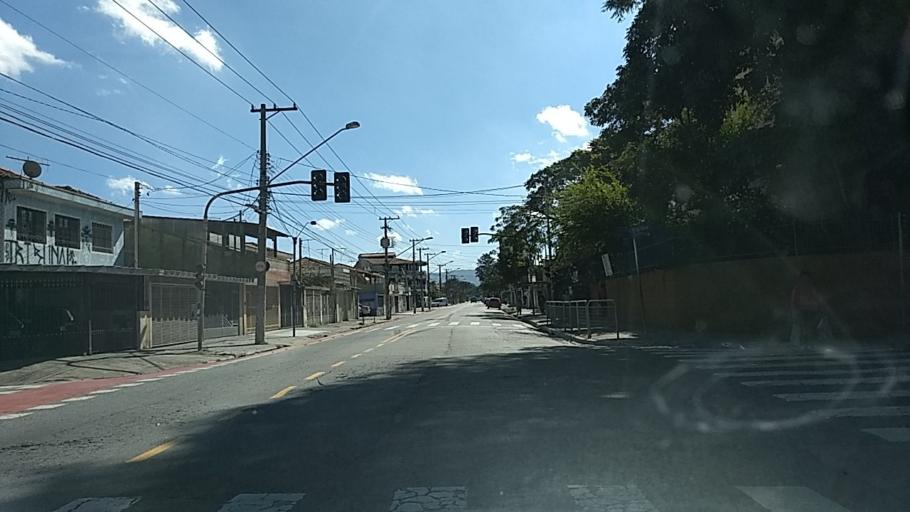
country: BR
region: Sao Paulo
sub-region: Guarulhos
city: Guarulhos
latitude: -23.4787
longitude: -46.5681
